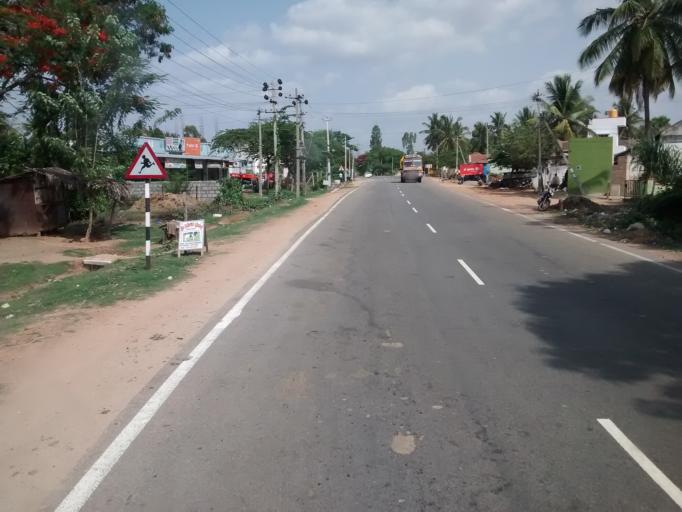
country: IN
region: Karnataka
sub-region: Mysore
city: Hunsur
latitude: 12.3646
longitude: 76.4193
